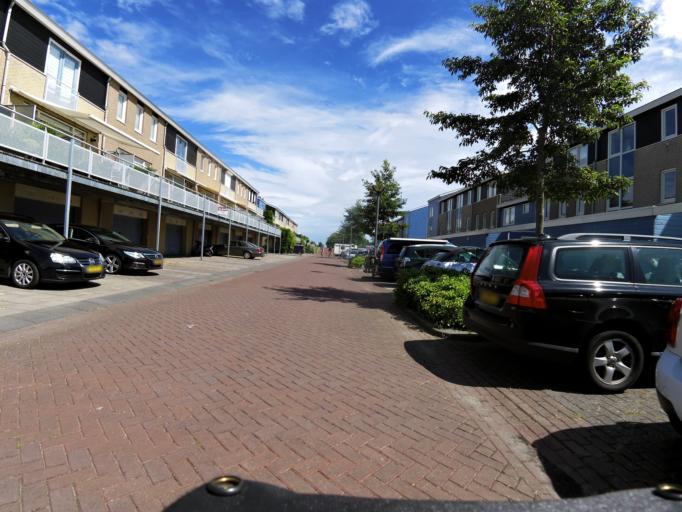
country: NL
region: Zeeland
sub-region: Gemeente Goes
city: Goes
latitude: 51.5549
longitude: 3.8056
